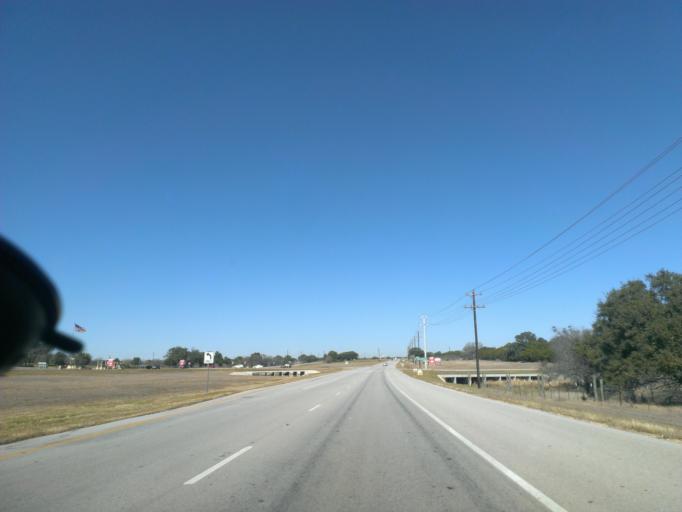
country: US
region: Texas
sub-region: Williamson County
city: Leander
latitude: 30.6259
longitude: -97.8629
